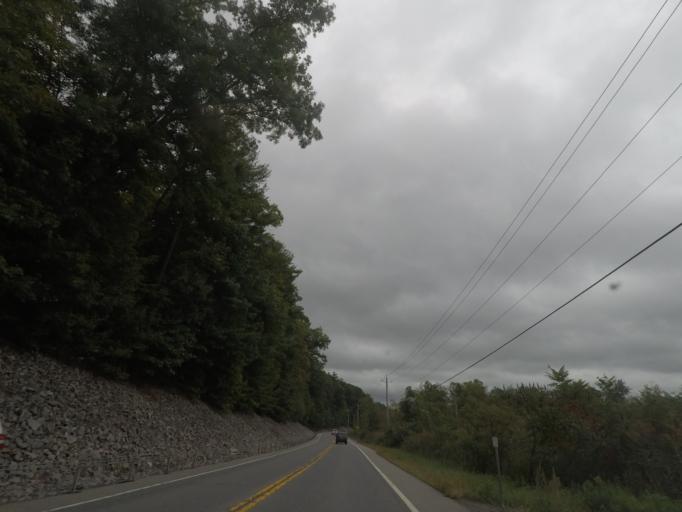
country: US
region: New York
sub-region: Saratoga County
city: Mechanicville
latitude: 42.9234
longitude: -73.7404
